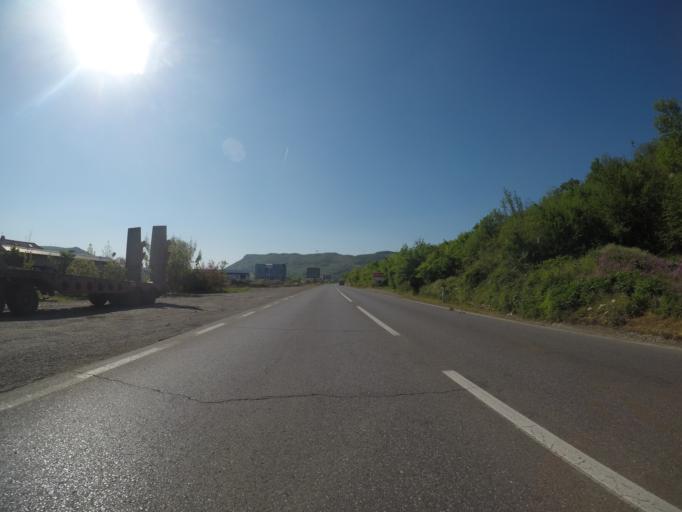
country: ME
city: Spuz
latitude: 42.4728
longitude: 19.1728
